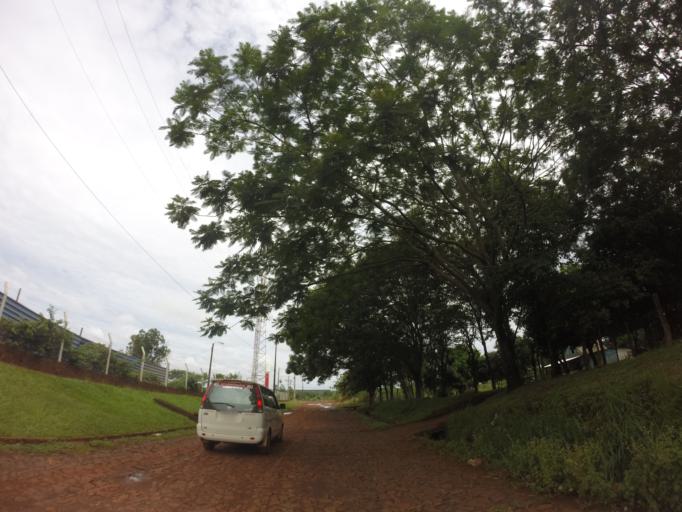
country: PY
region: Alto Parana
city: Ciudad del Este
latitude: -25.3812
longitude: -54.6604
